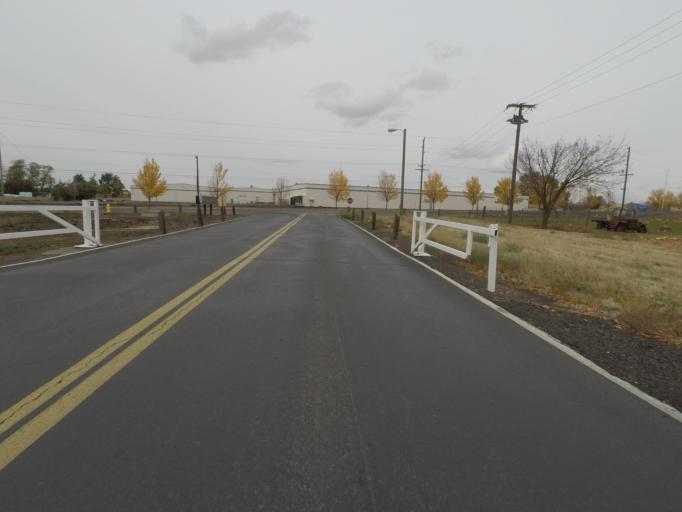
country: US
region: Washington
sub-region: Walla Walla County
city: Walla Walla East
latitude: 46.0817
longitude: -118.2749
